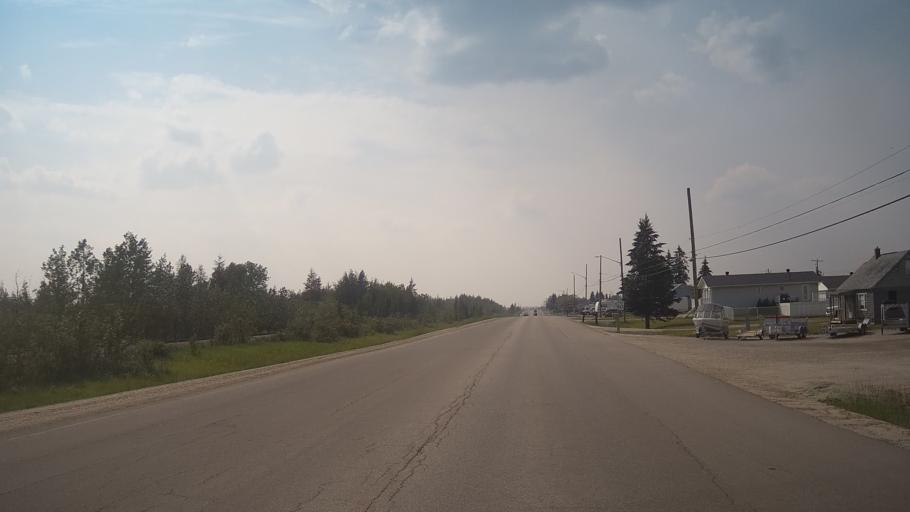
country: CA
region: Ontario
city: Kapuskasing
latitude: 49.4011
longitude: -82.3808
